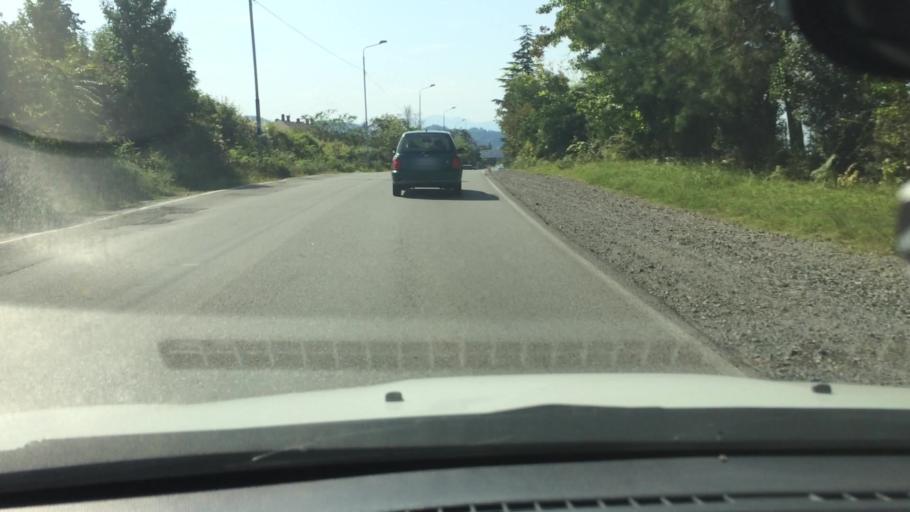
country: GE
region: Ajaria
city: Makhinjauri
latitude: 41.7385
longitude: 41.7353
